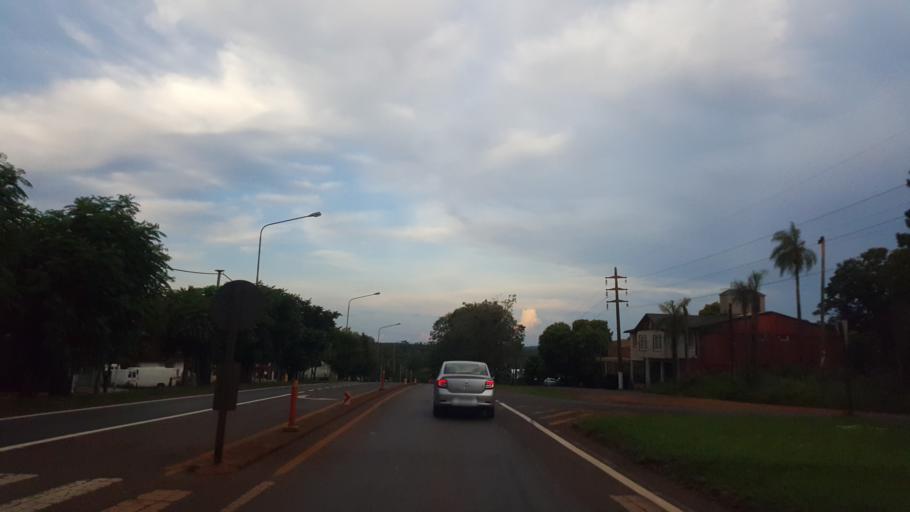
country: AR
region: Misiones
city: Jardin America
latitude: -27.0362
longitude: -55.2264
